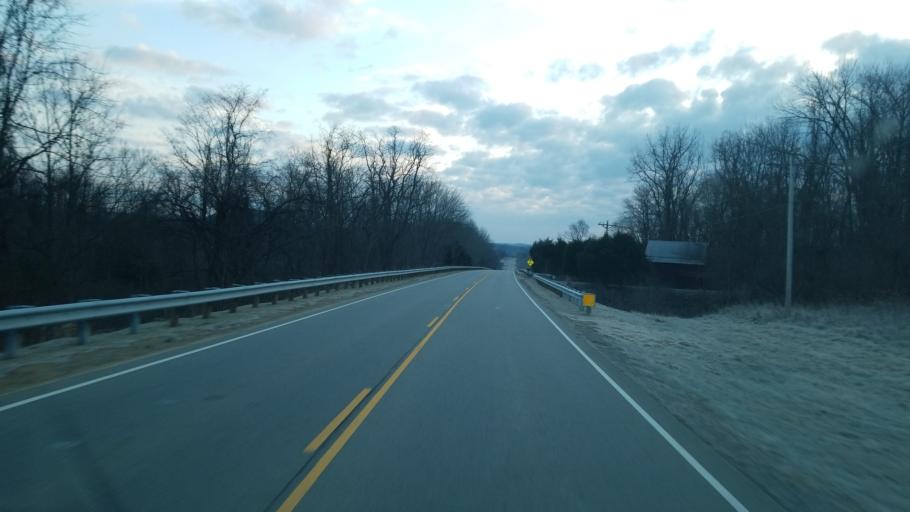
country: US
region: Ohio
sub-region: Highland County
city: Greenfield
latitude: 39.2305
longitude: -83.3556
